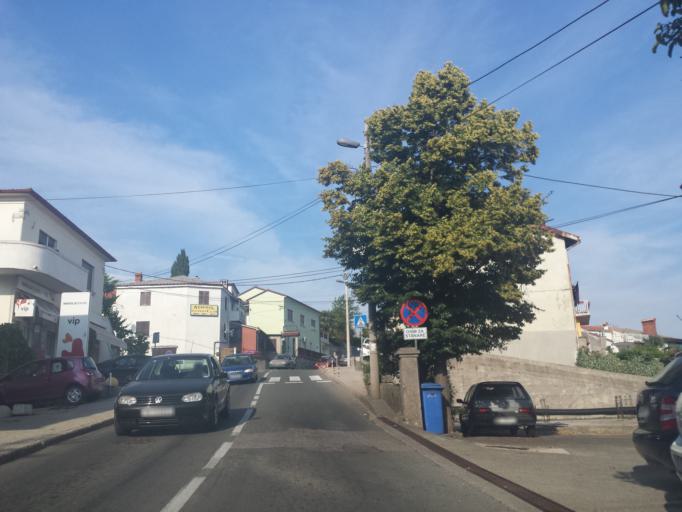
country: HR
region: Primorsko-Goranska
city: Matulji
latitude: 45.3641
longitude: 14.3263
